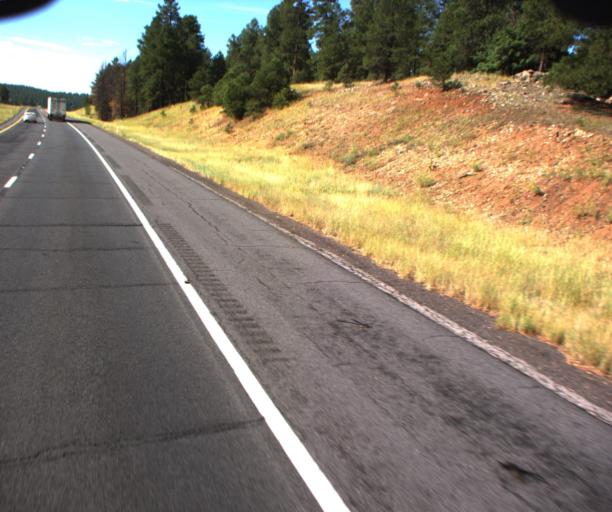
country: US
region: Arizona
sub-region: Coconino County
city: Kachina Village
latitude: 35.1107
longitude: -111.6817
